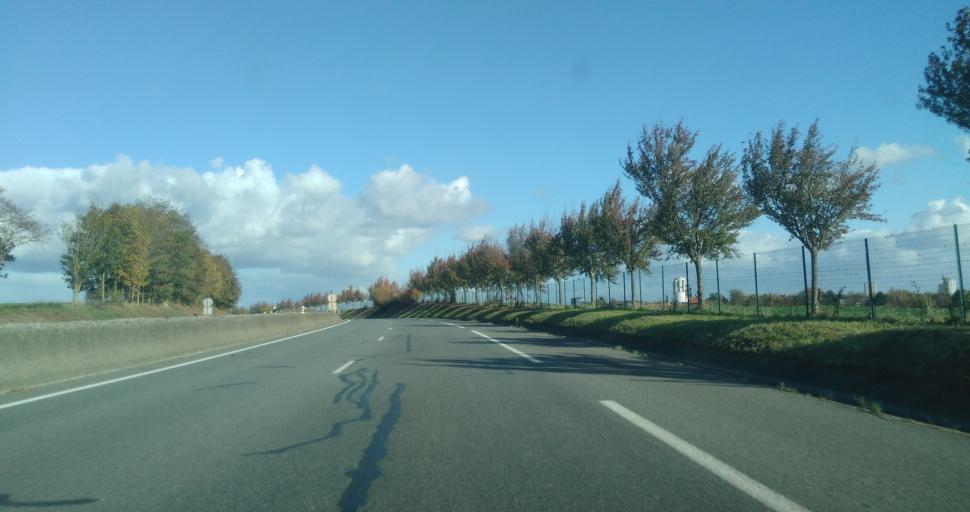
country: FR
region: Nord-Pas-de-Calais
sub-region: Departement du Pas-de-Calais
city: Dainville
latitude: 50.2909
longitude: 2.7179
